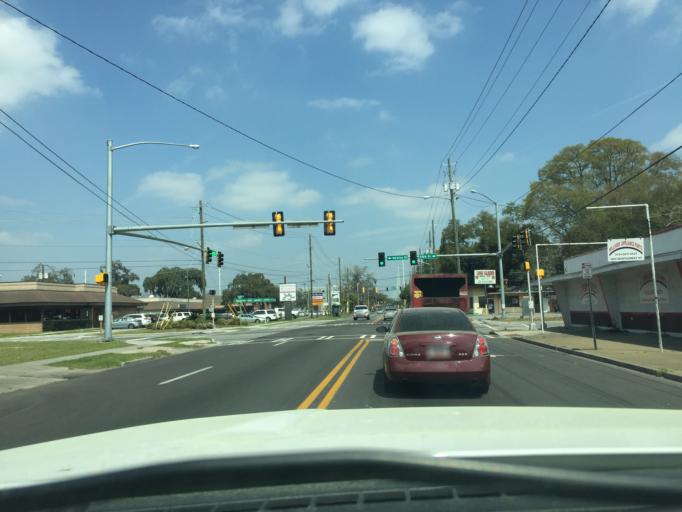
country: US
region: Georgia
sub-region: Chatham County
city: Savannah
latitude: 32.0443
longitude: -81.1097
